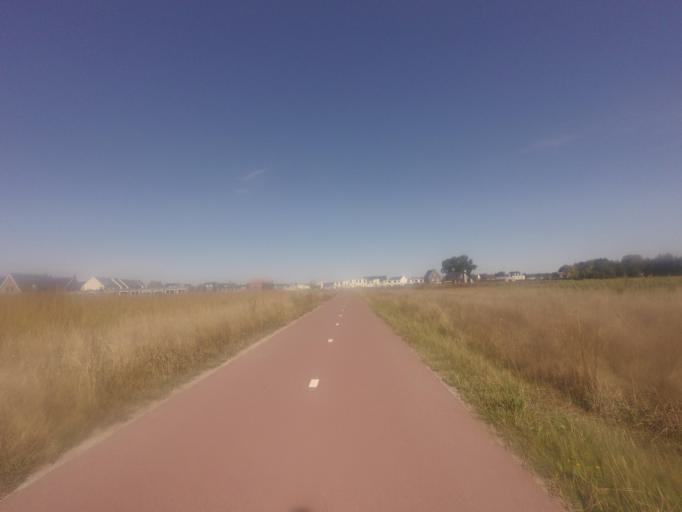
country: NL
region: North Brabant
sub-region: Gemeente Veldhoven
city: Oerle
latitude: 51.4056
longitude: 5.3780
